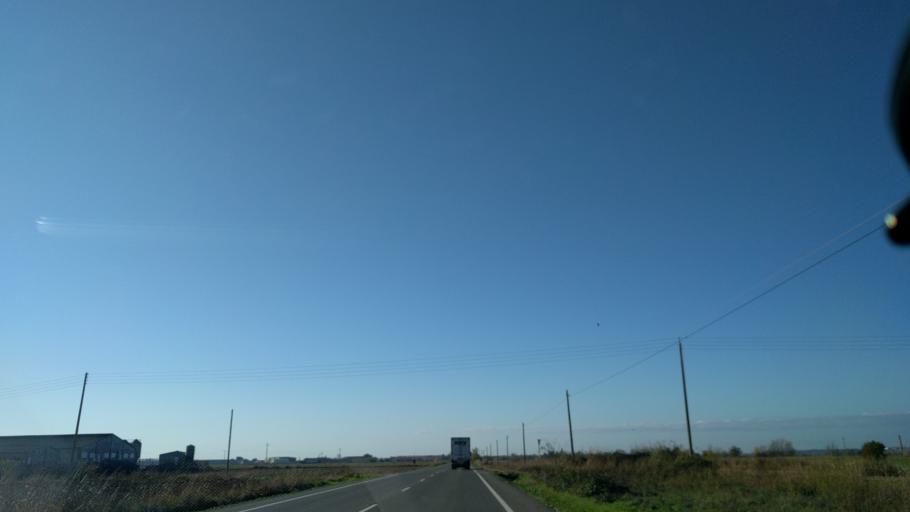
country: ES
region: Catalonia
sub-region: Provincia de Lleida
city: Termens
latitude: 41.7311
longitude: 0.7785
